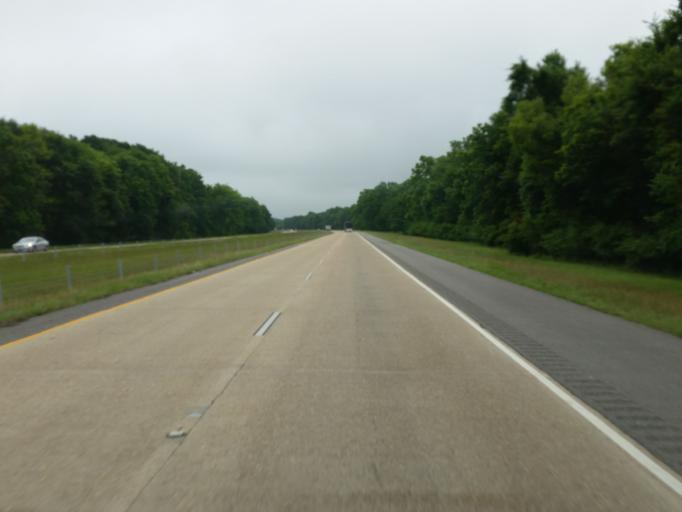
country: US
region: Louisiana
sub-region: Madison Parish
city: Tallulah
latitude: 32.3397
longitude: -91.0695
